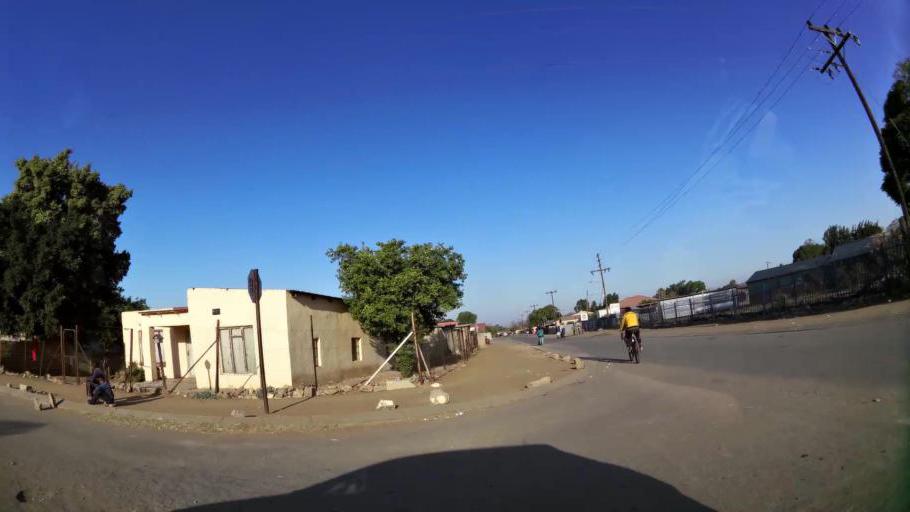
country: ZA
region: North-West
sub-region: Bojanala Platinum District Municipality
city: Rustenburg
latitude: -25.6397
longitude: 27.2197
